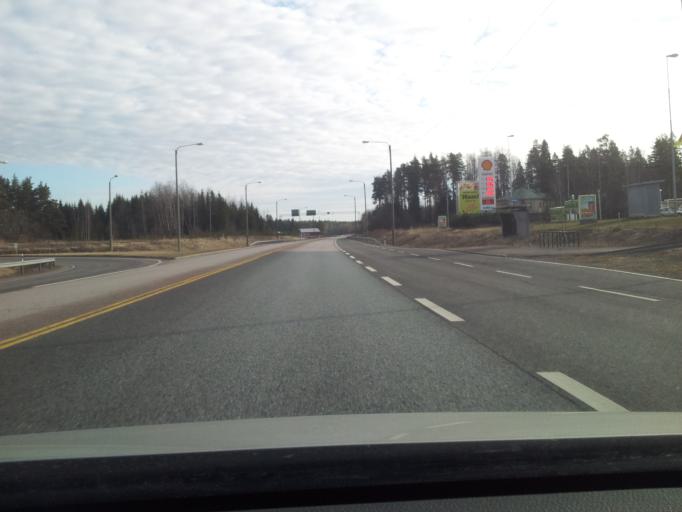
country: FI
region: Uusimaa
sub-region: Loviisa
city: Liljendal
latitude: 60.5612
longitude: 26.0547
